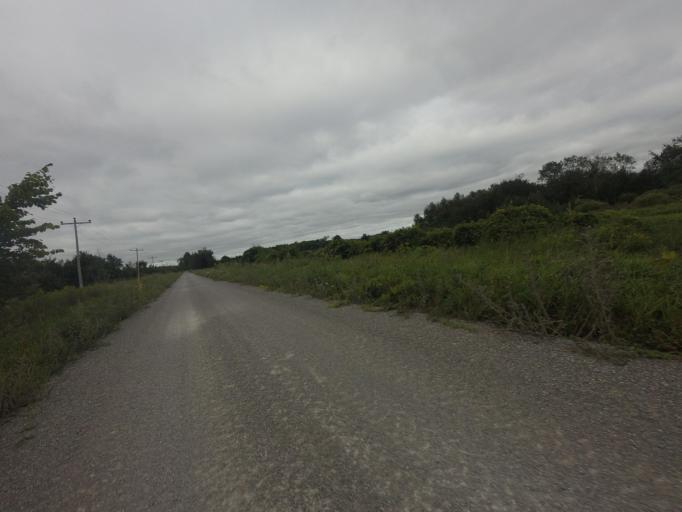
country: CA
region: Ontario
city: Omemee
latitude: 44.4596
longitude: -78.7591
